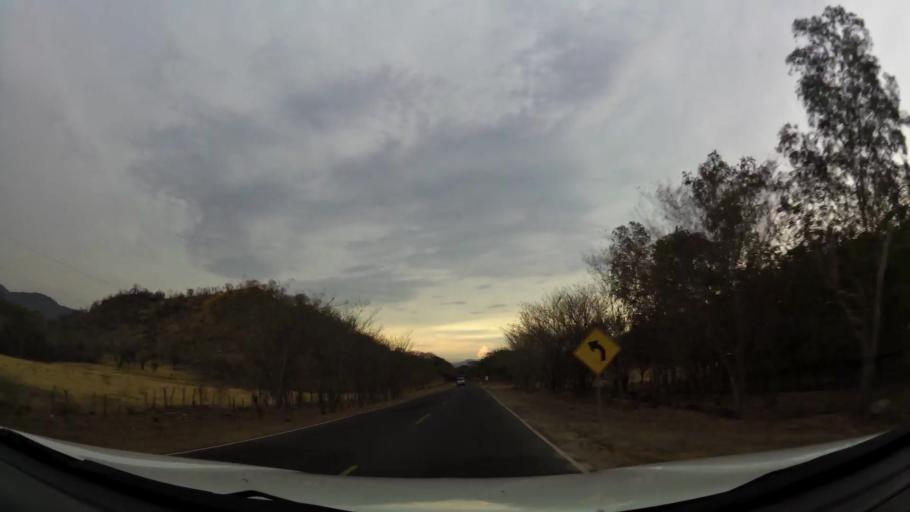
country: NI
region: Leon
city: La Jicaral
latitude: 12.7017
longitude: -86.4001
